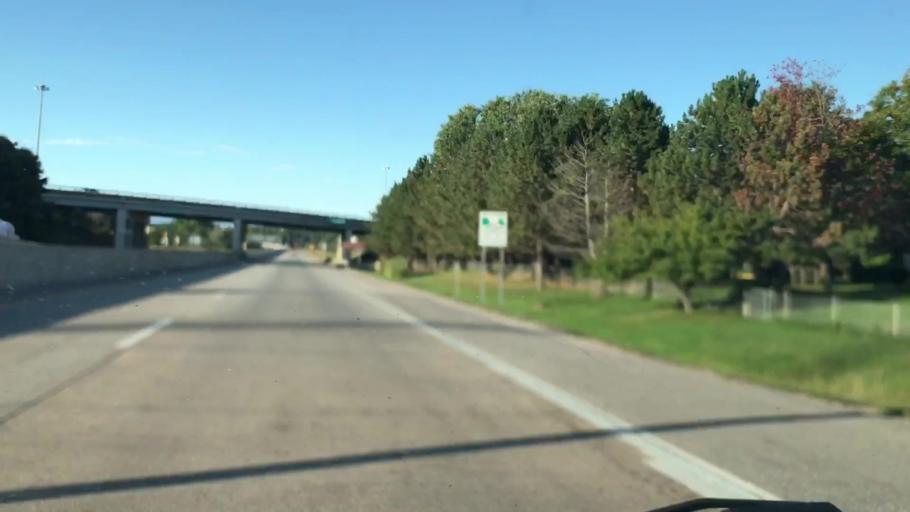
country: US
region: Michigan
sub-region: Chippewa County
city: Sault Ste. Marie
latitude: 46.4927
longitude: -84.3700
